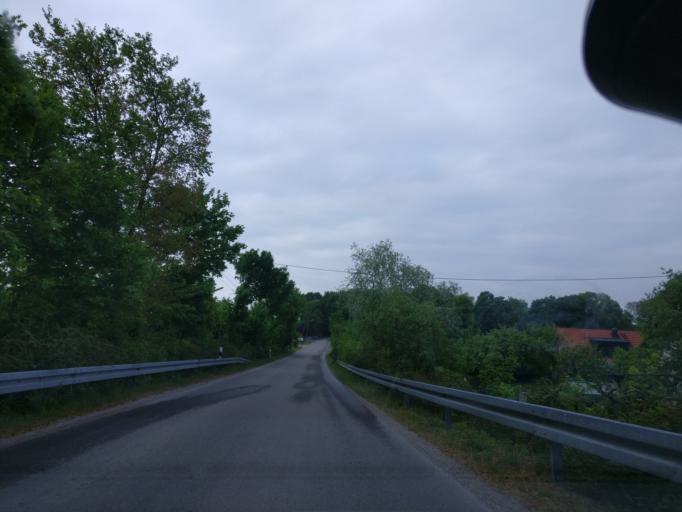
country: DE
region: Bavaria
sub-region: Upper Bavaria
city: Karlsfeld
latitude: 48.2030
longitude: 11.4318
